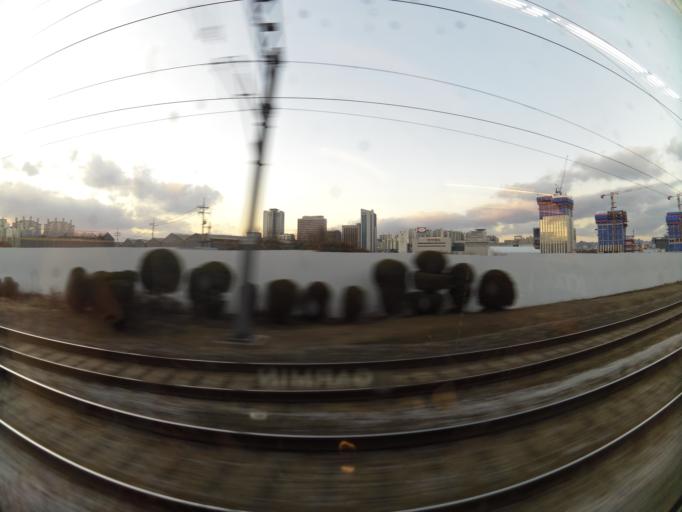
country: KR
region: Seoul
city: Seoul
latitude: 37.5280
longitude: 126.9615
